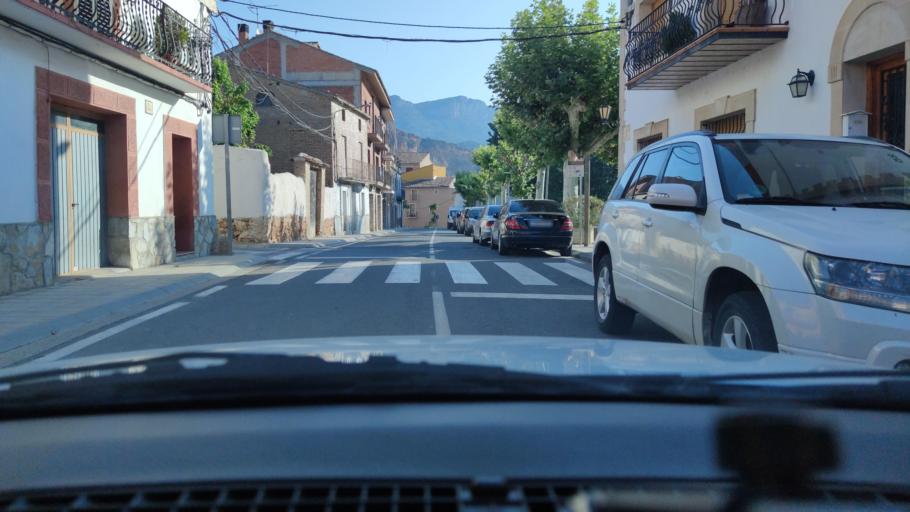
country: ES
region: Catalonia
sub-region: Provincia de Lleida
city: Camarasa
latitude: 41.8678
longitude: 0.8411
